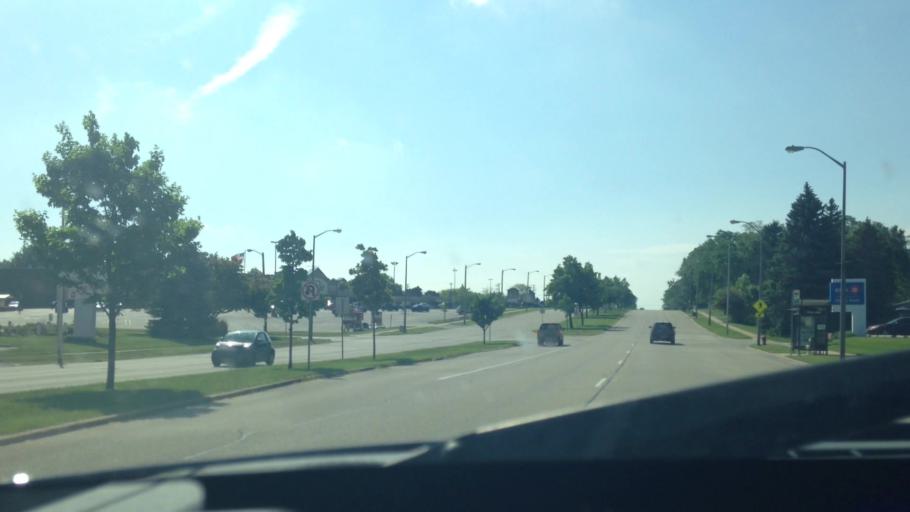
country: US
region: Wisconsin
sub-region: Waukesha County
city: Menomonee Falls
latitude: 43.1676
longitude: -88.1013
